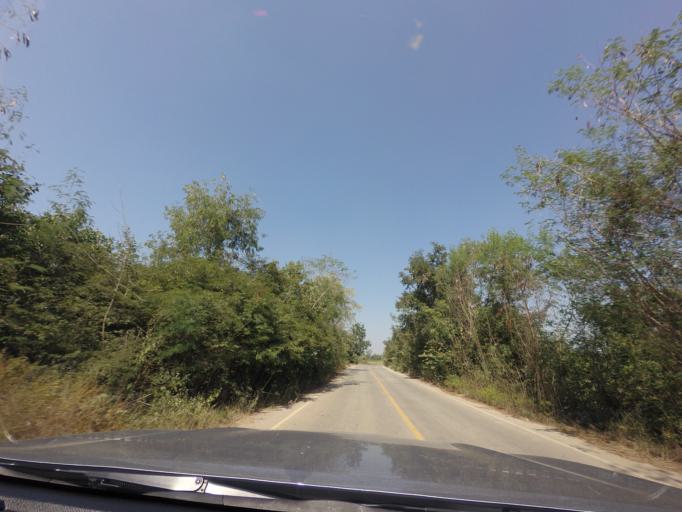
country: TH
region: Sukhothai
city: Si Samrong
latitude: 17.1452
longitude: 99.7698
